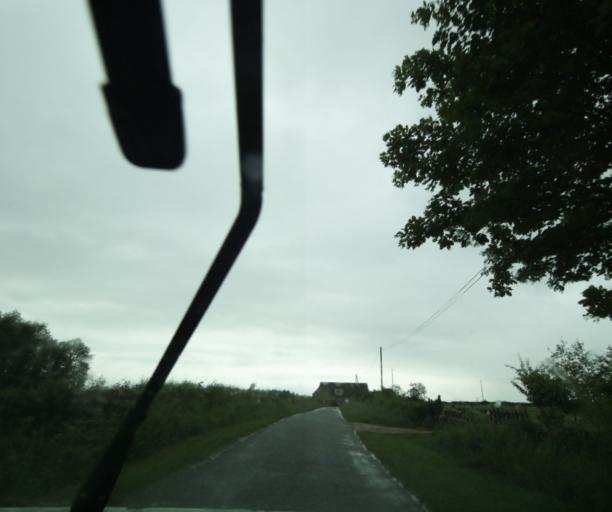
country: FR
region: Bourgogne
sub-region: Departement de Saone-et-Loire
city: Ciry-le-Noble
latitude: 46.5328
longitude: 4.3020
